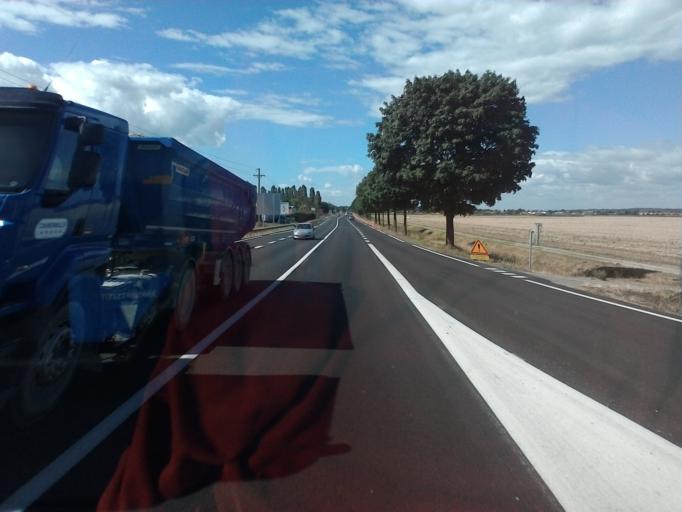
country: FR
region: Rhone-Alpes
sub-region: Departement de l'Ain
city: Amberieu-en-Bugey
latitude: 45.9700
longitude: 5.3405
